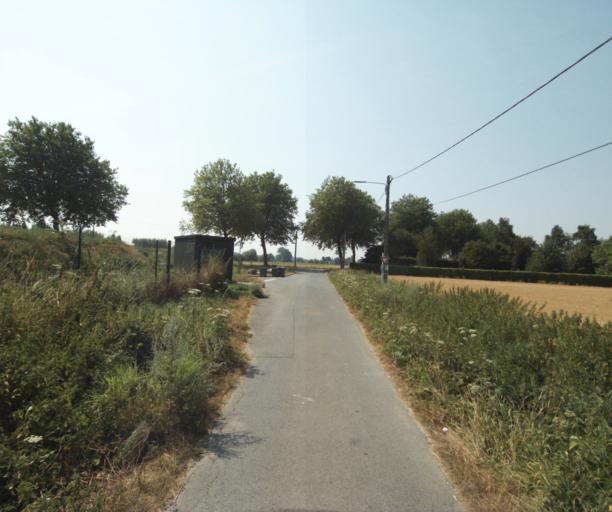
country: FR
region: Nord-Pas-de-Calais
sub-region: Departement du Nord
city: Quesnoy-sur-Deule
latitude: 50.7184
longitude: 3.0138
